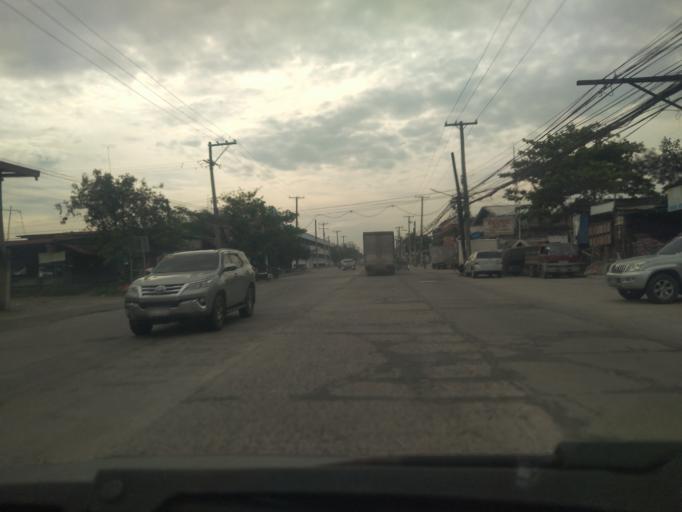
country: PH
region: Central Luzon
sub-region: Province of Pampanga
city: San Fernando
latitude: 15.0207
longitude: 120.6995
